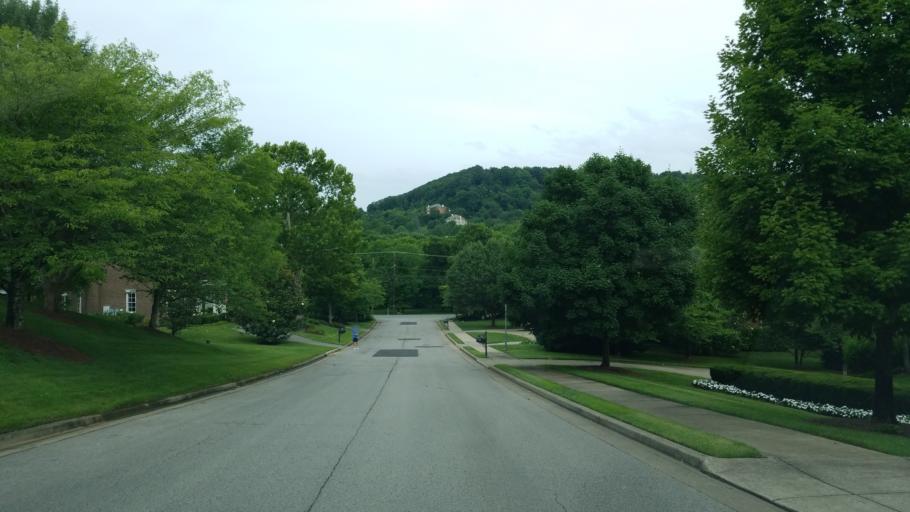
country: US
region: Tennessee
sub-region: Davidson County
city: Forest Hills
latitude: 36.0563
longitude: -86.8143
